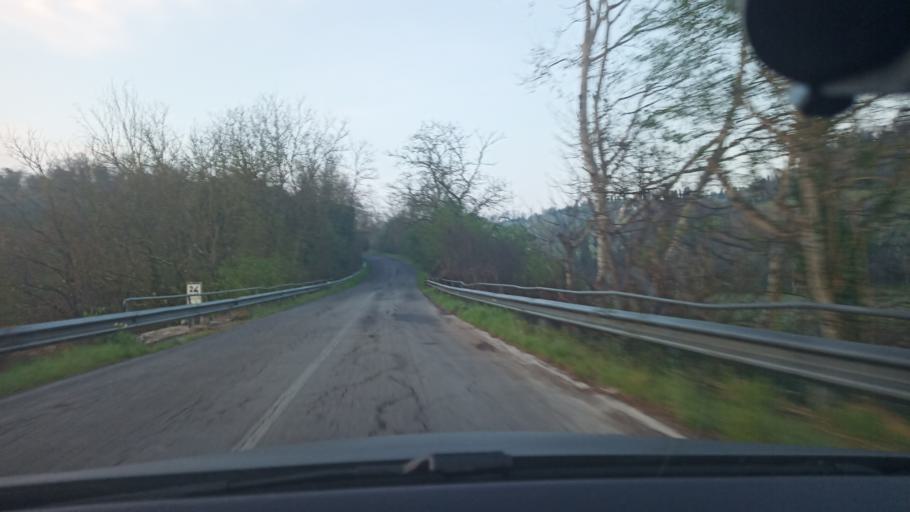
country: IT
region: Latium
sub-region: Provincia di Rieti
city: Cantalupo in Sabina
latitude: 42.3261
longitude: 12.6423
